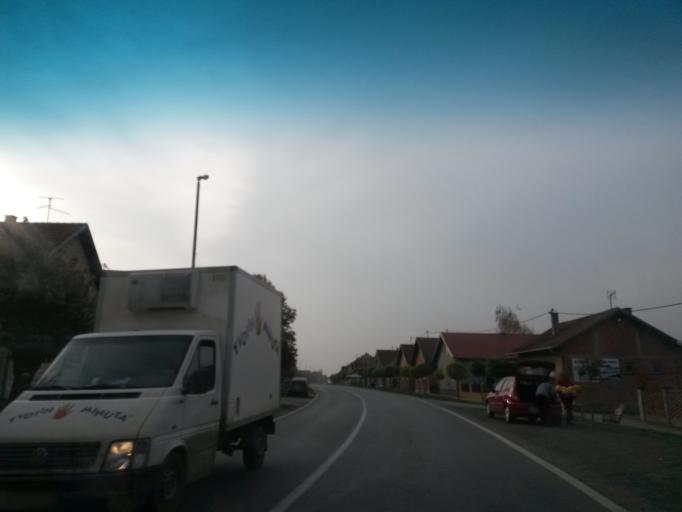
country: HR
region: Vukovarsko-Srijemska
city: Nustar
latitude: 45.3338
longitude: 18.8492
